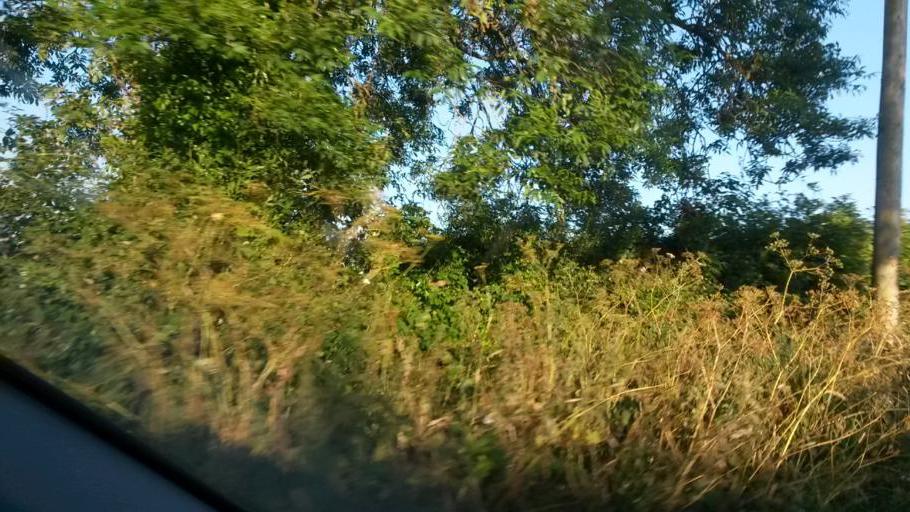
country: IE
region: Leinster
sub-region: An Mhi
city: Ashbourne
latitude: 53.5543
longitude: -6.3590
